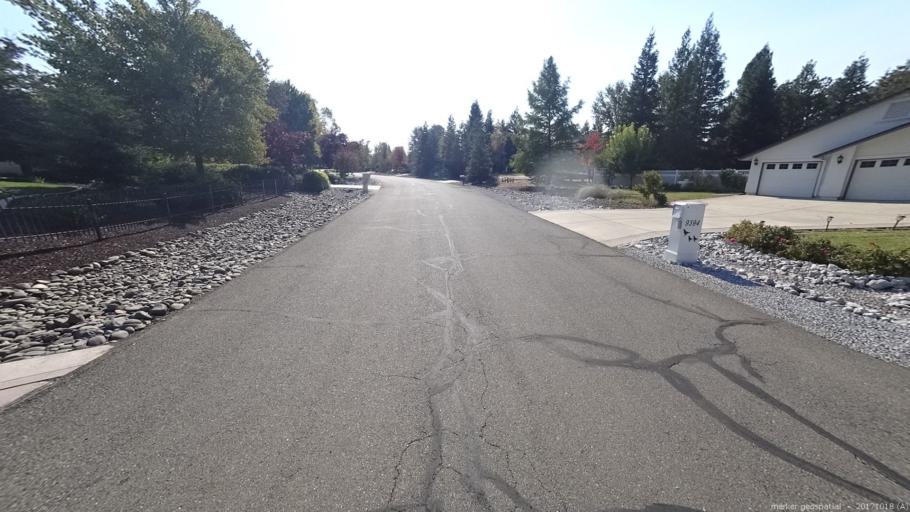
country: US
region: California
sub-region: Shasta County
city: Palo Cedro
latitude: 40.5591
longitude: -122.2356
